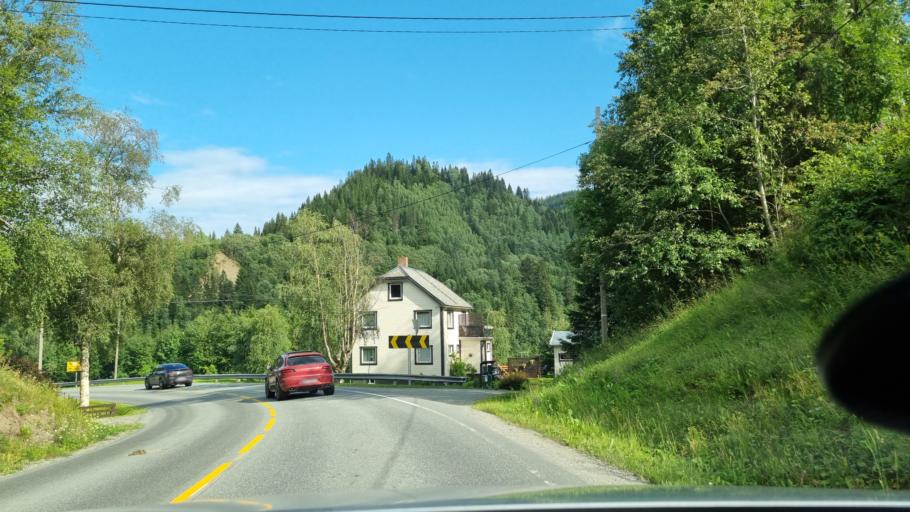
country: NO
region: Sor-Trondelag
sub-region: Midtre Gauldal
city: Storen
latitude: 62.9927
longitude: 10.4923
